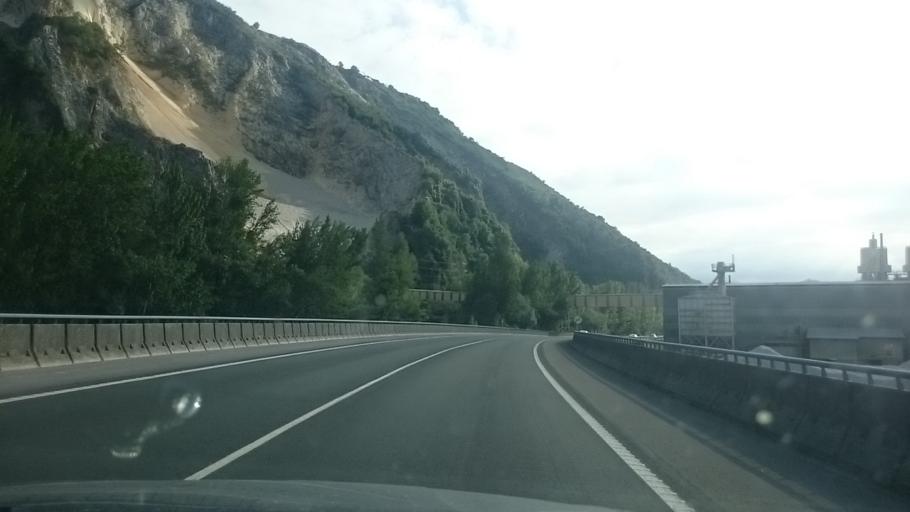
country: ES
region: Asturias
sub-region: Province of Asturias
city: Oviedo
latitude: 43.3299
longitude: -5.7725
